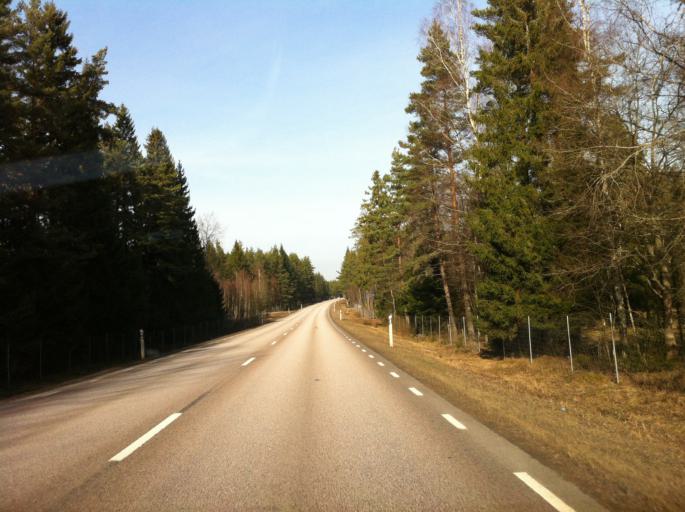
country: SE
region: Vaestra Goetaland
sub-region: Tidaholms Kommun
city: Tidaholm
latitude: 58.1305
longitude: 13.8953
